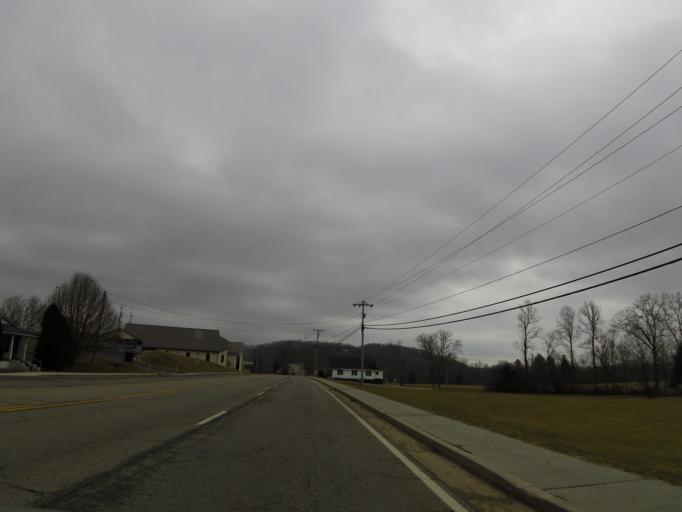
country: US
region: Tennessee
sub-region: Scott County
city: Huntsville
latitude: 36.4141
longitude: -84.4958
